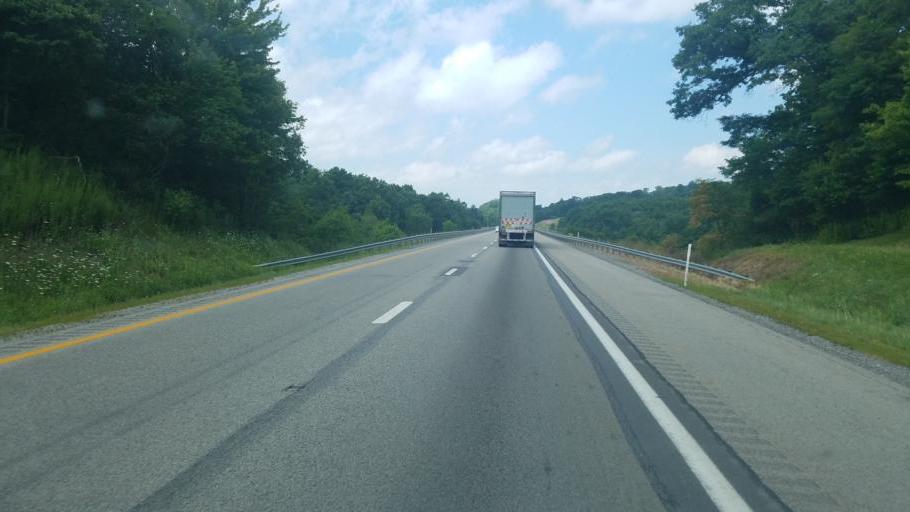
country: US
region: West Virginia
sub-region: Raleigh County
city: Shady Spring
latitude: 37.6452
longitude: -81.1088
